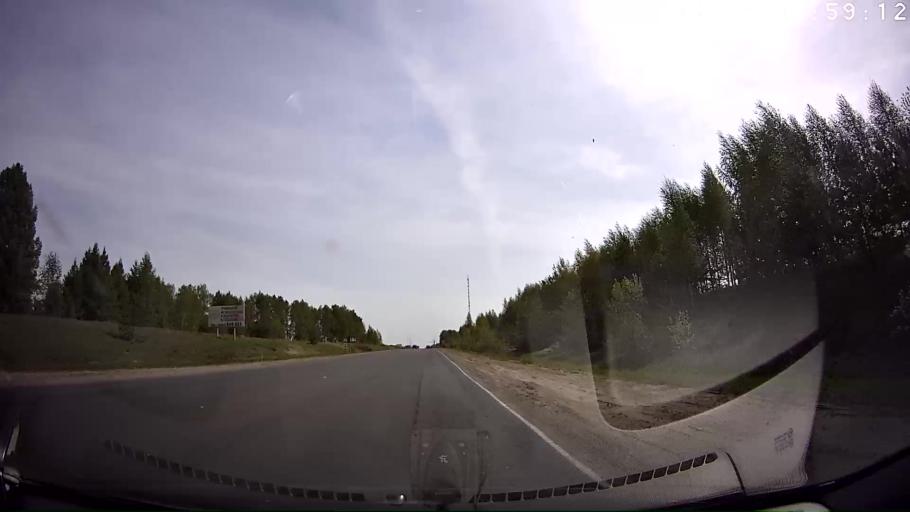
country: RU
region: Mariy-El
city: Sovetskiy
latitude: 56.7519
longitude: 48.5038
